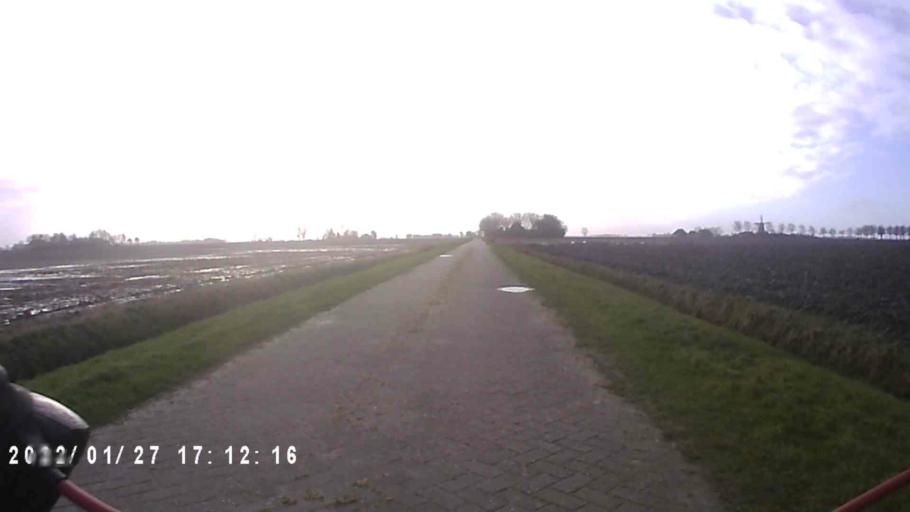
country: NL
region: Friesland
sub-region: Gemeente Dongeradeel
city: Anjum
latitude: 53.3992
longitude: 6.0961
